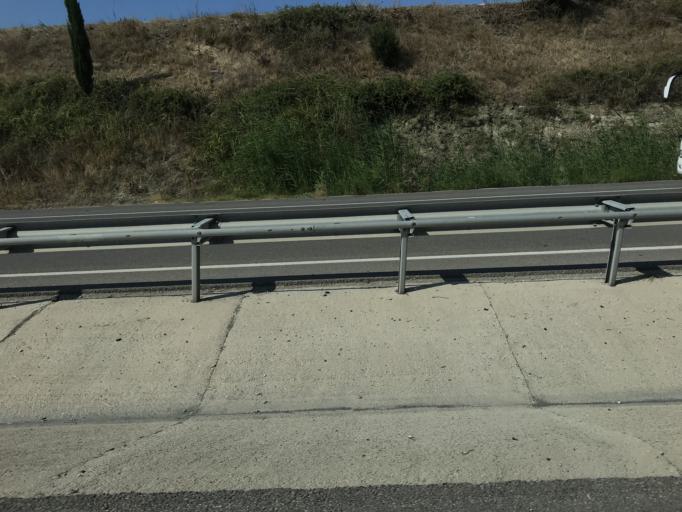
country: TR
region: Bursa
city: Mahmudiye
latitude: 40.2083
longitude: 28.5976
